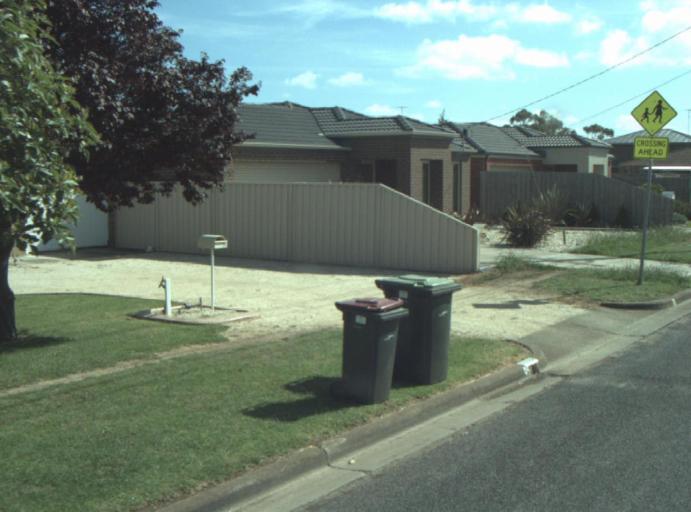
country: AU
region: Victoria
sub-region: Greater Geelong
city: Lara
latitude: -38.0161
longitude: 144.4080
